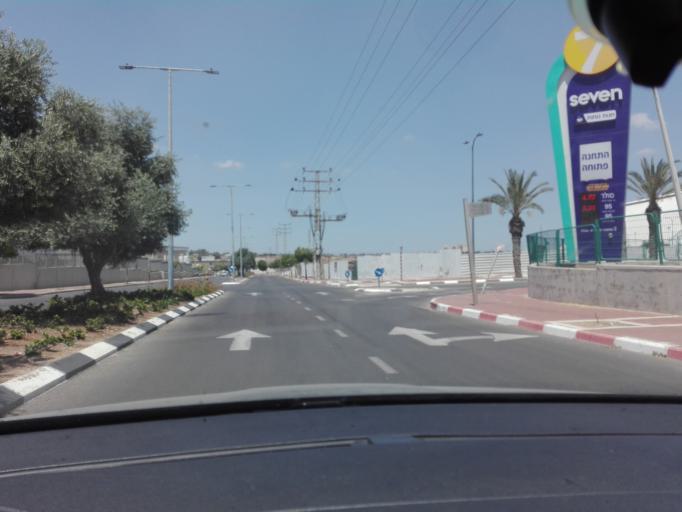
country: IL
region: Southern District
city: Qiryat Gat
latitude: 31.5951
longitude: 34.7821
